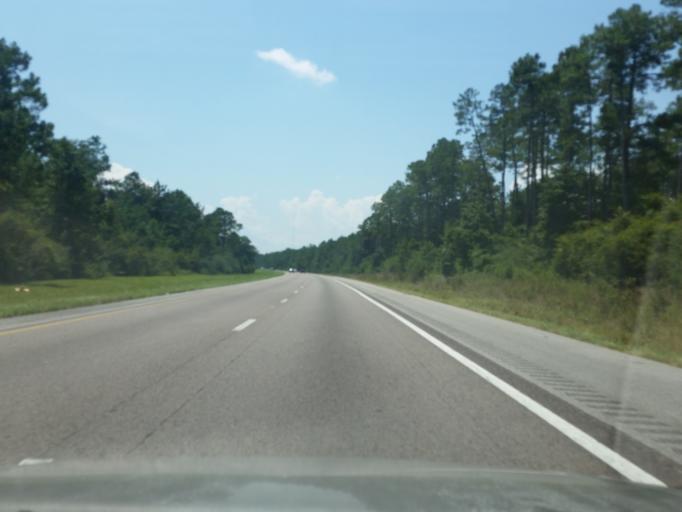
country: US
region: Florida
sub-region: Escambia County
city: Cantonment
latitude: 30.5814
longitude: -87.4850
